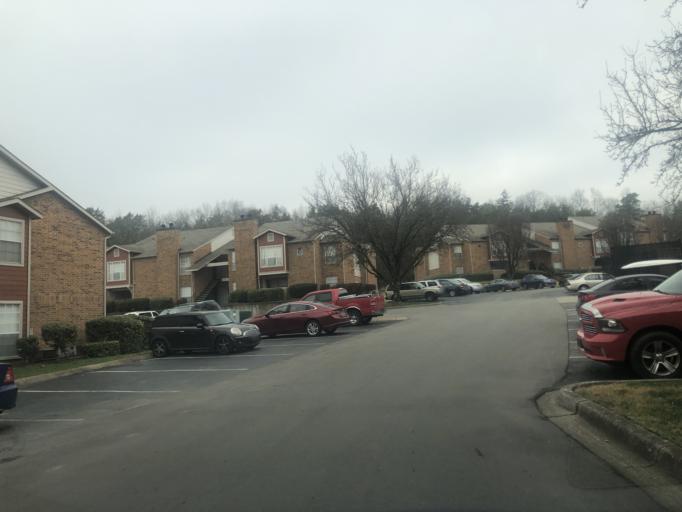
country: US
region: Tennessee
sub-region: Rutherford County
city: La Vergne
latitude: 36.0635
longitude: -86.6433
